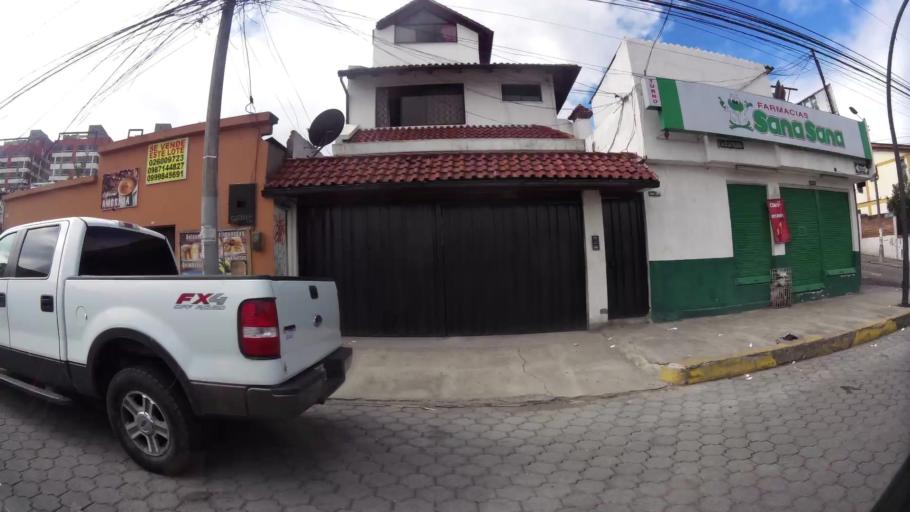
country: EC
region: Pichincha
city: Quito
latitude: -0.1560
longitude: -78.4700
